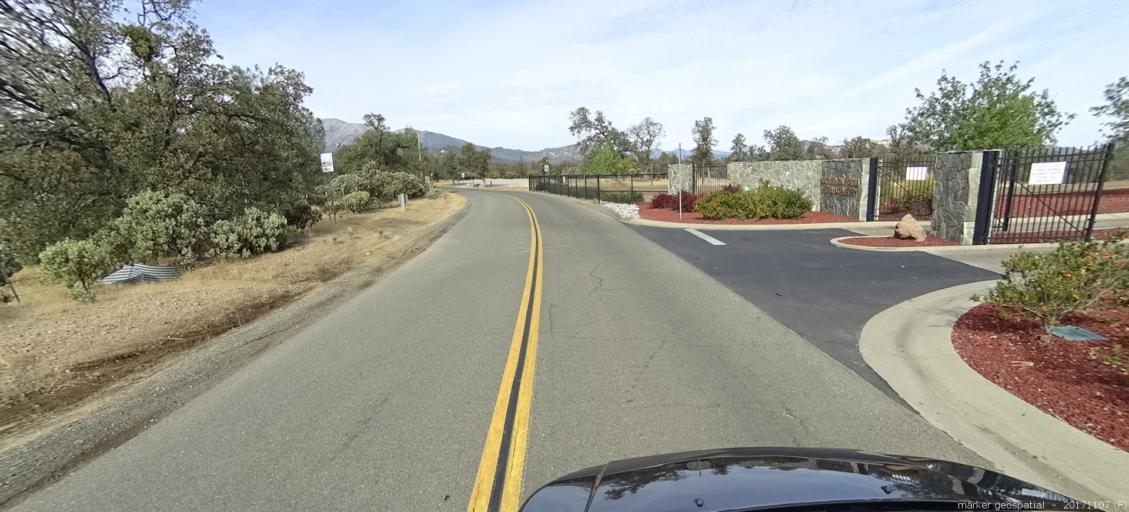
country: US
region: California
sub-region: Shasta County
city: Shasta
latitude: 40.4784
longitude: -122.5445
